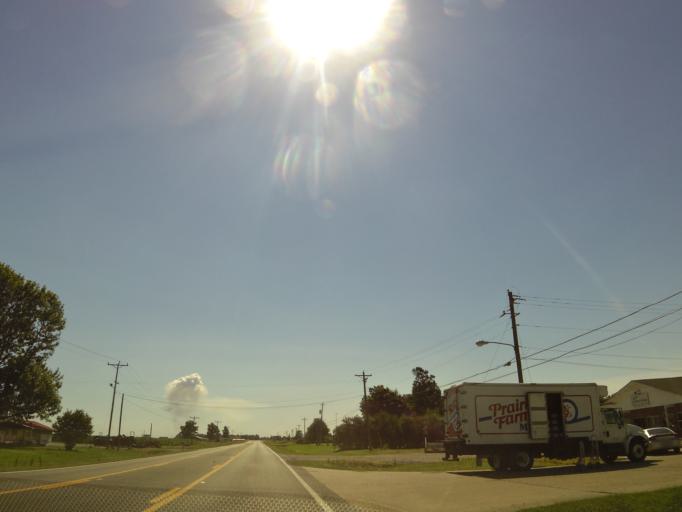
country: US
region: Arkansas
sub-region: Clay County
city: Piggott
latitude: 36.3818
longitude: -90.1756
